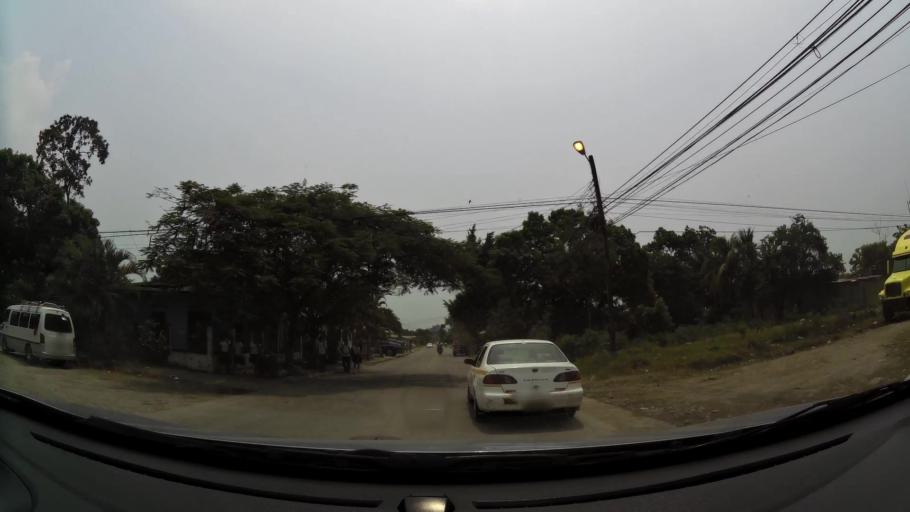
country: HN
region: Yoro
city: El Progreso
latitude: 15.3879
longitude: -87.7985
